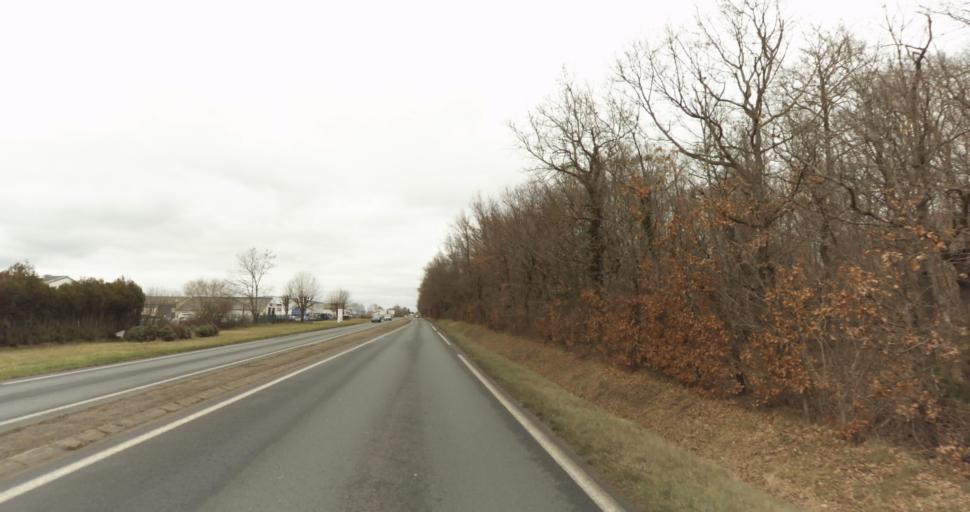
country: FR
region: Pays de la Loire
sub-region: Departement de Maine-et-Loire
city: Vivy
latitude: 47.3354
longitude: -0.0650
